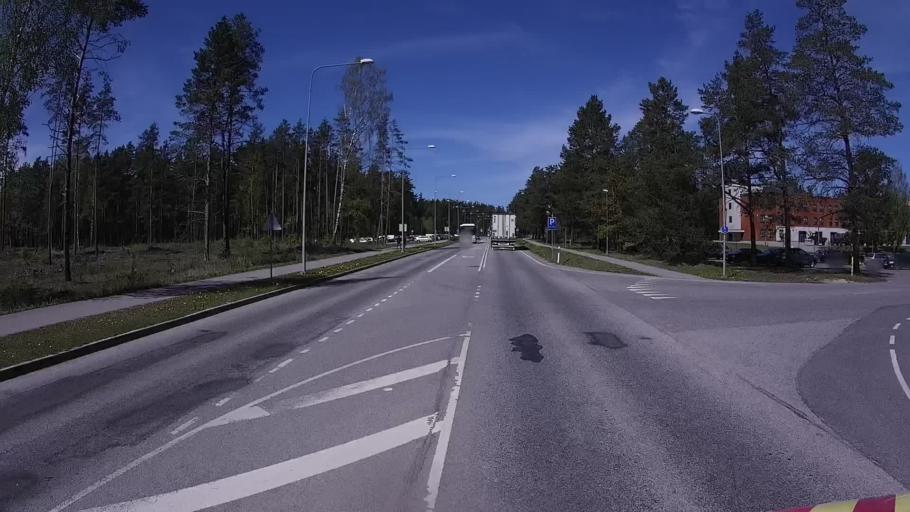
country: EE
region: Vorumaa
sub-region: Voru linn
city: Voru
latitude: 57.8216
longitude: 27.0207
